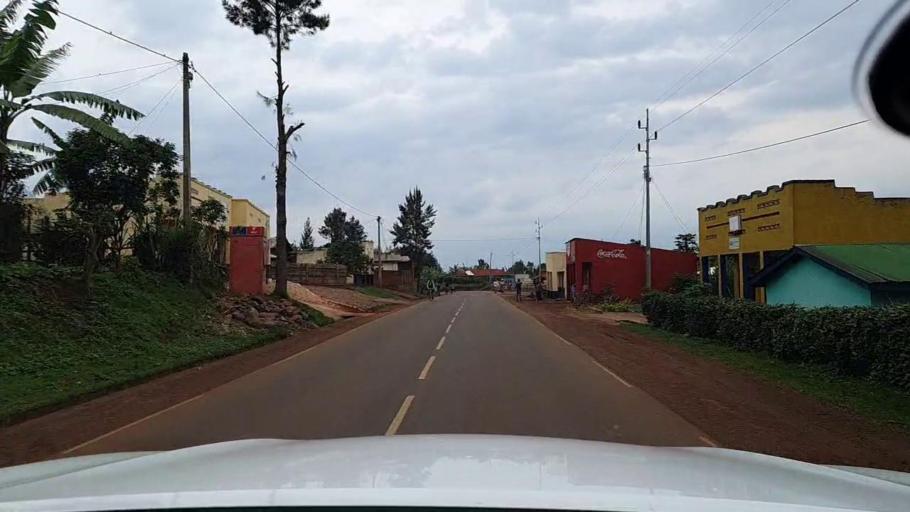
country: RW
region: Western Province
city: Cyangugu
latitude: -2.6432
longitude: 28.9535
